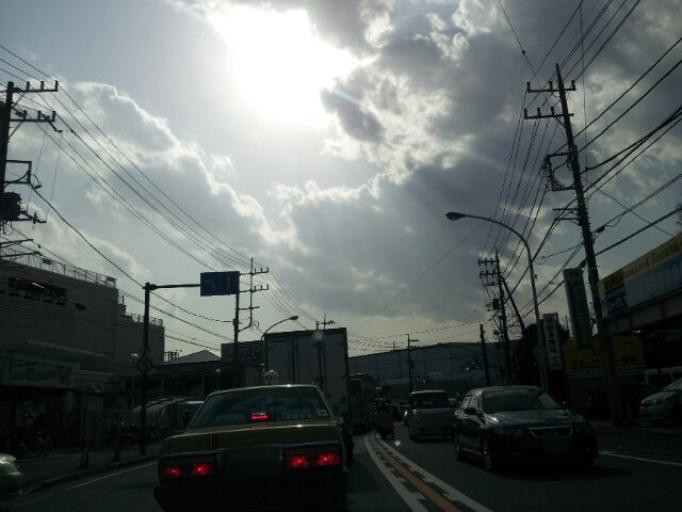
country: JP
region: Kanagawa
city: Yokohama
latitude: 35.4206
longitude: 139.5630
